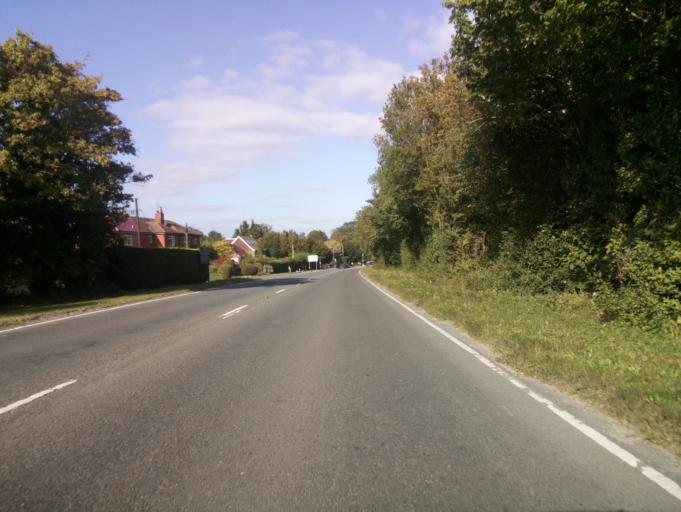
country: GB
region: England
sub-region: Hampshire
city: Basingstoke
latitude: 51.2948
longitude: -1.1153
